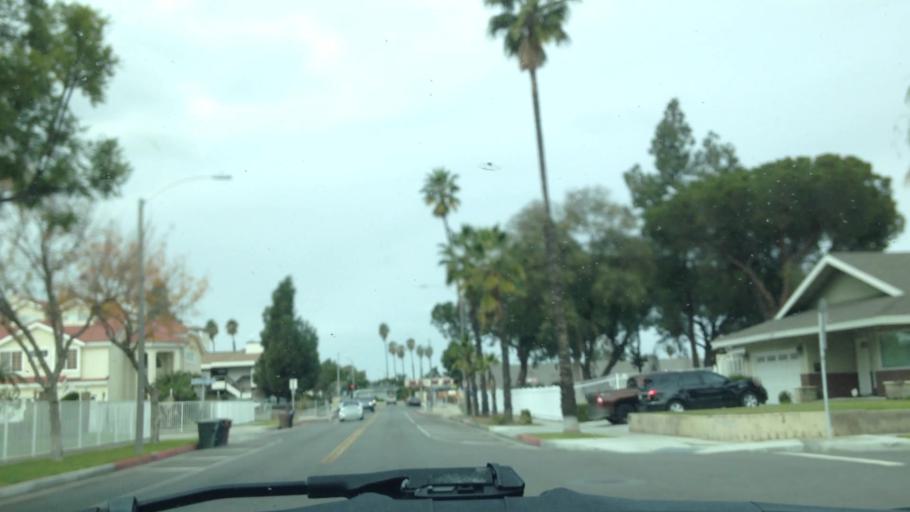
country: US
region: California
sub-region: Orange County
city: Anaheim
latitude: 33.8454
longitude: -117.9313
